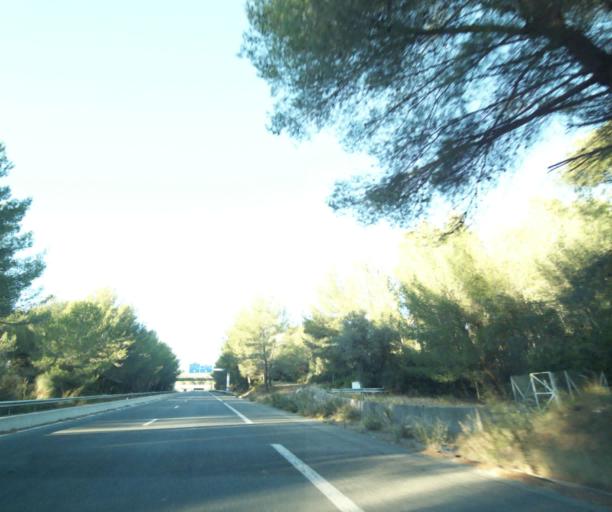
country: FR
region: Provence-Alpes-Cote d'Azur
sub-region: Departement du Var
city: Saint-Cyr-sur-Mer
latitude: 43.1903
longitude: 5.6912
